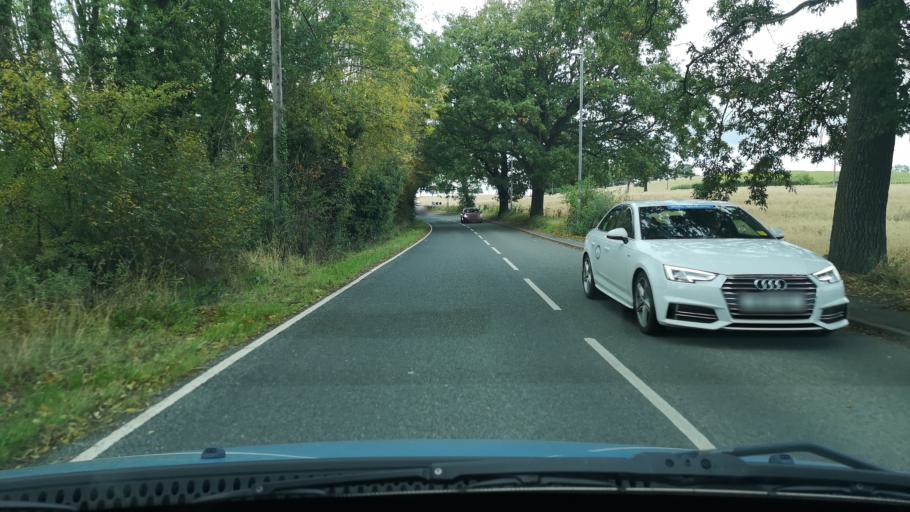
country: GB
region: England
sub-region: City and Borough of Wakefield
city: Low Ackworth
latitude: 53.6596
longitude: -1.3400
